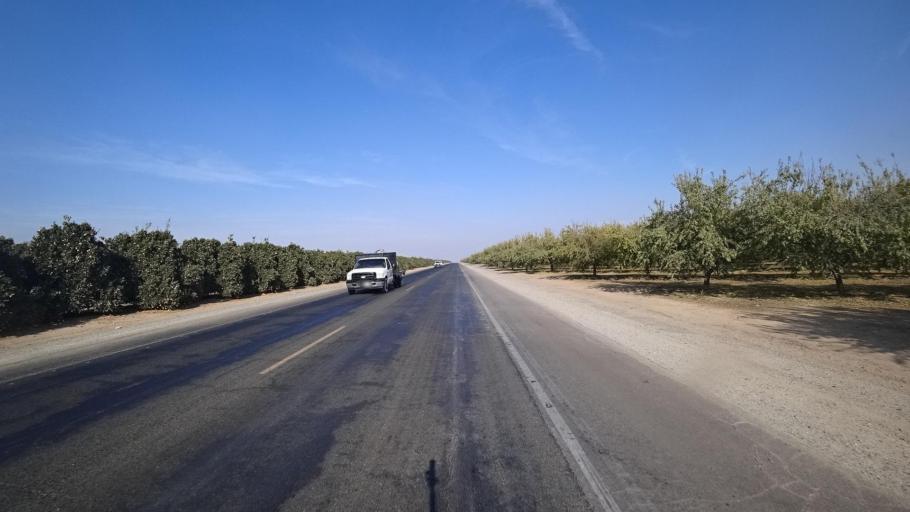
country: US
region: California
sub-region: Kern County
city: McFarland
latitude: 35.6950
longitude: -119.1738
